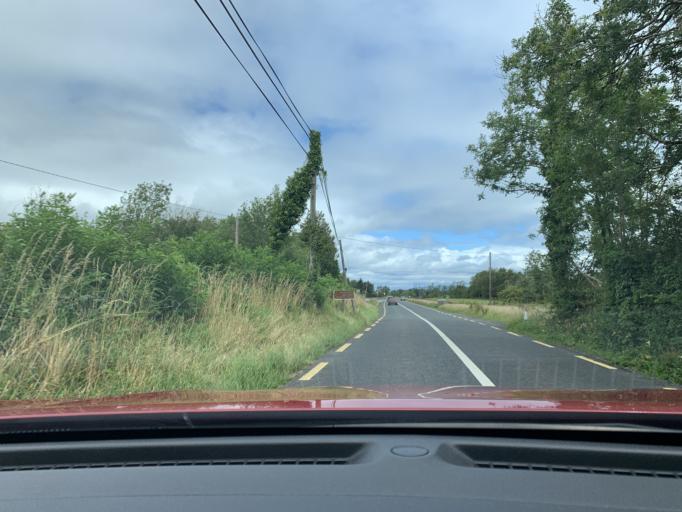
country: IE
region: Connaught
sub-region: County Leitrim
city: Carrick-on-Shannon
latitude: 53.9080
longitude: -8.1303
